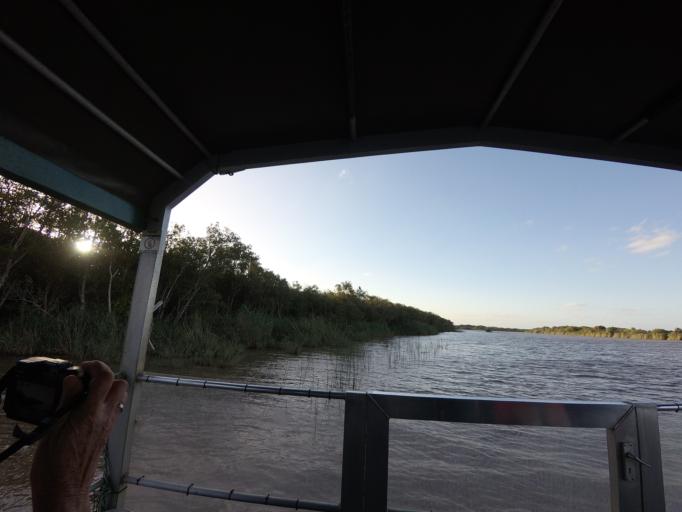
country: ZA
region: KwaZulu-Natal
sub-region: uMkhanyakude District Municipality
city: Mtubatuba
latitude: -28.3449
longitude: 32.4083
